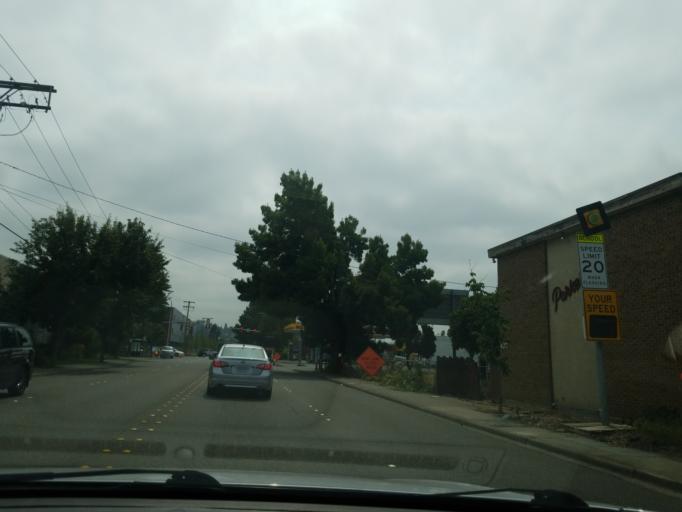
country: US
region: Washington
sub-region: King County
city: Renton
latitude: 47.4895
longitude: -122.2022
